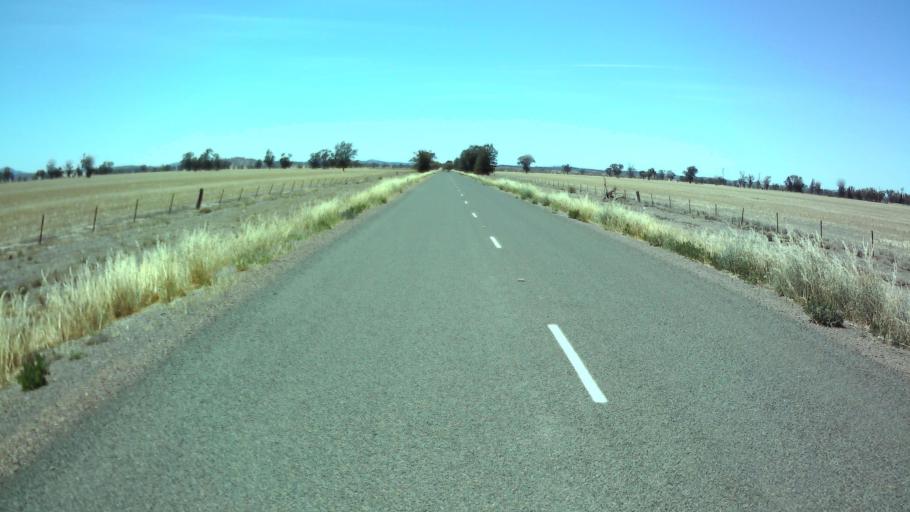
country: AU
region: New South Wales
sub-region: Bland
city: West Wyalong
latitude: -33.6597
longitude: 147.5956
